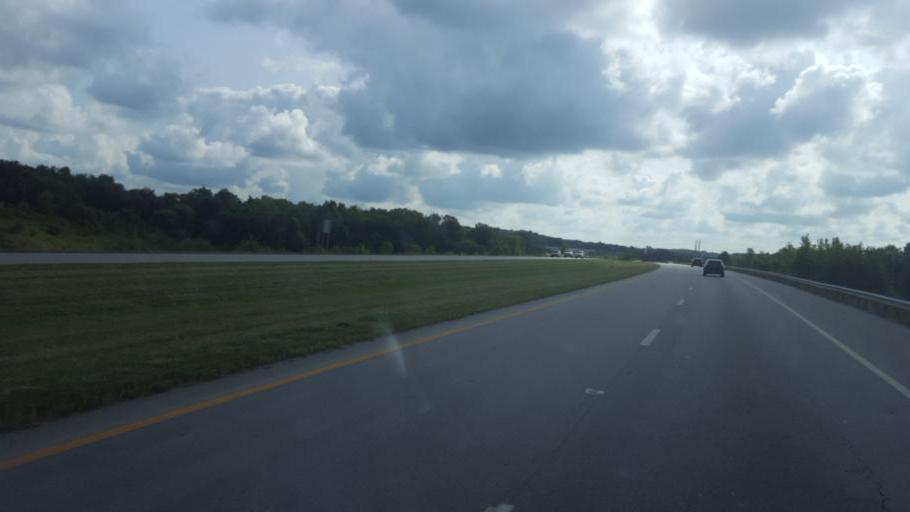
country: US
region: Ohio
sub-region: Stark County
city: Canton
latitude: 40.7843
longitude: -81.3336
